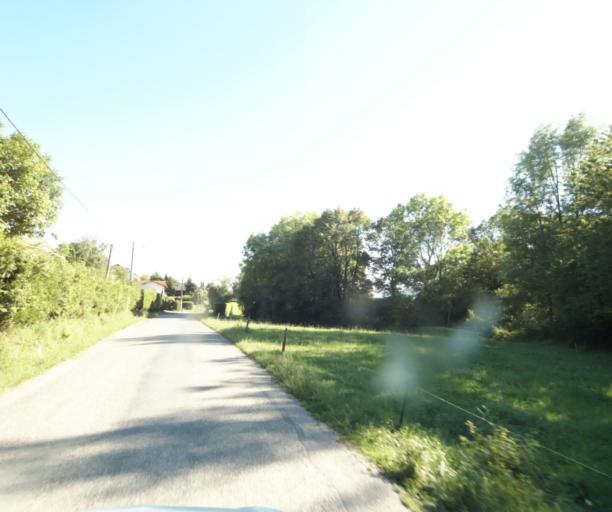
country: FR
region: Rhone-Alpes
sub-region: Departement de la Haute-Savoie
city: Ballaison
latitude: 46.3019
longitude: 6.3306
